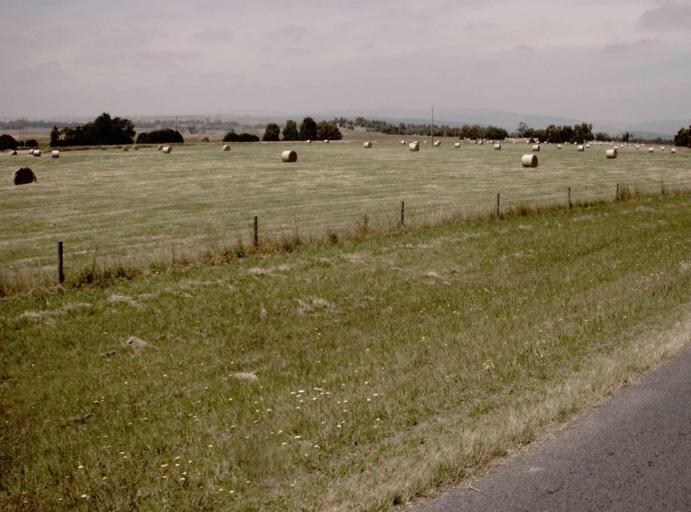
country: AU
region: Victoria
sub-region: Latrobe
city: Traralgon
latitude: -38.2273
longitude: 146.5420
